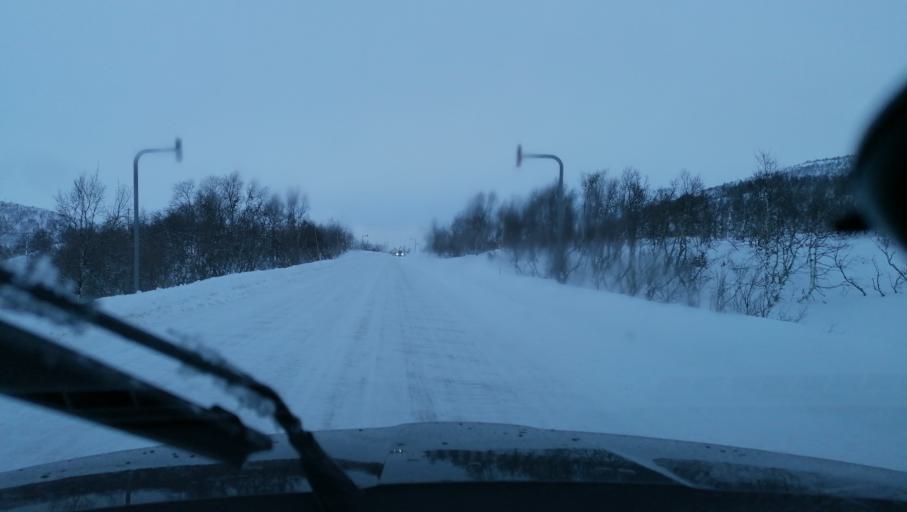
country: NO
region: Aust-Agder
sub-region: Bykle
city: Hovden
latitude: 59.6323
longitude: 7.4537
